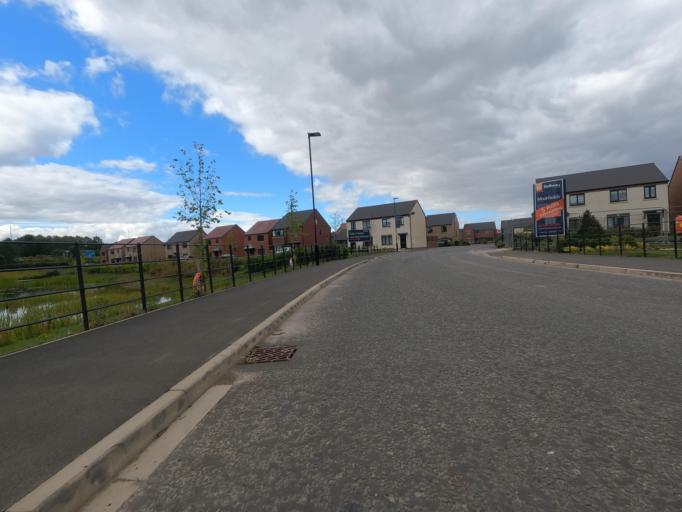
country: GB
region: England
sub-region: Newcastle upon Tyne
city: Gosforth
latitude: 55.0352
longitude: -1.5894
